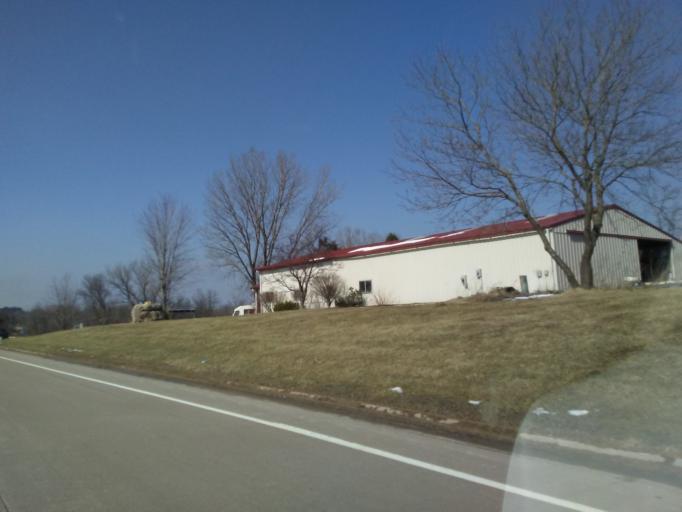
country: US
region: Wisconsin
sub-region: La Crosse County
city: West Salem
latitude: 43.7145
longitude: -91.0705
